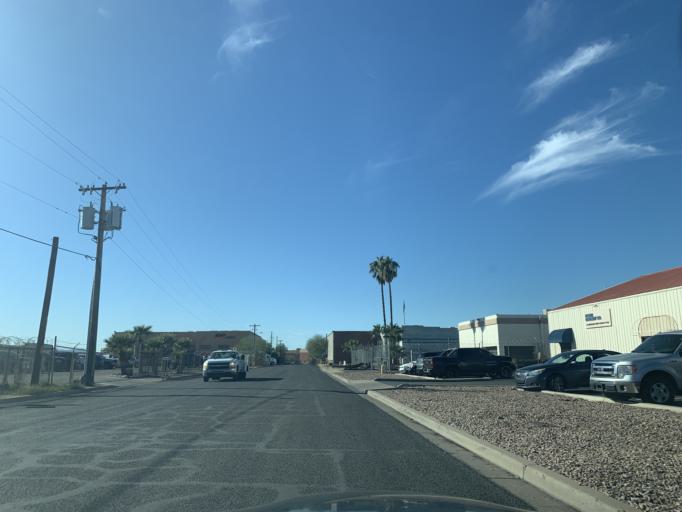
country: US
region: Arizona
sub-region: Maricopa County
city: Tempe Junction
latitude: 33.4183
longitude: -112.0002
